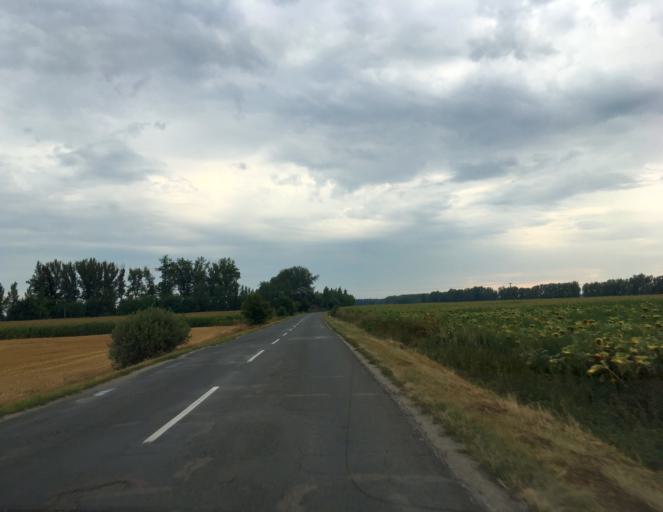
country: SK
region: Trnavsky
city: Gabcikovo
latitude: 47.8872
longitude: 17.6630
